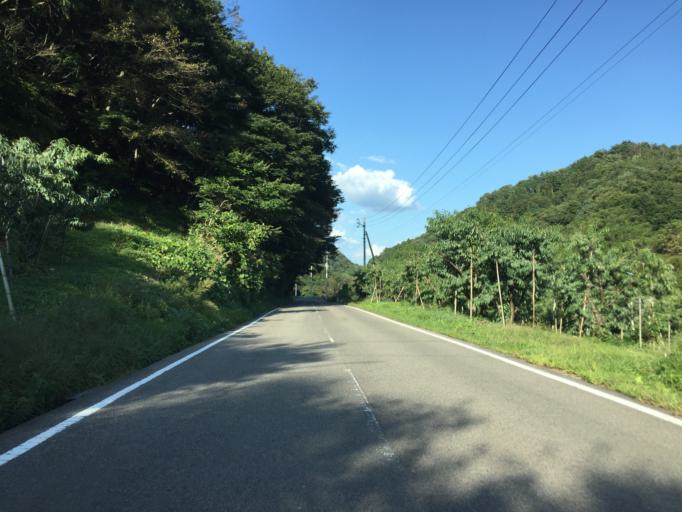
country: JP
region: Fukushima
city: Fukushima-shi
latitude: 37.7392
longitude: 140.5435
